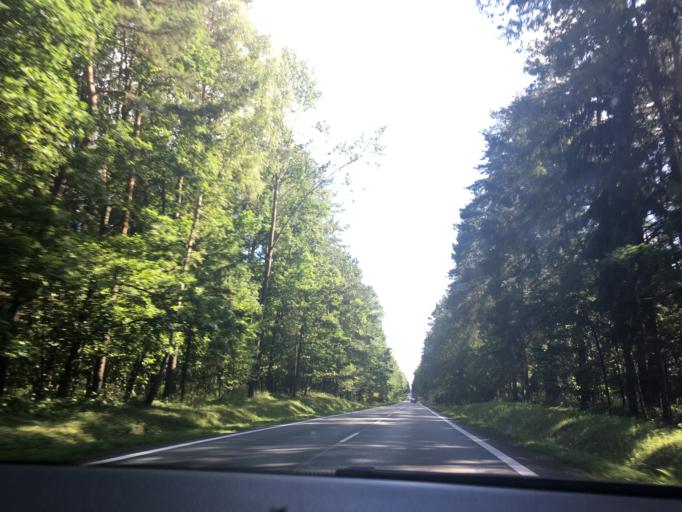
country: PL
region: Podlasie
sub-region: Powiat bialostocki
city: Wasilkow
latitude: 53.3100
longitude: 23.1266
